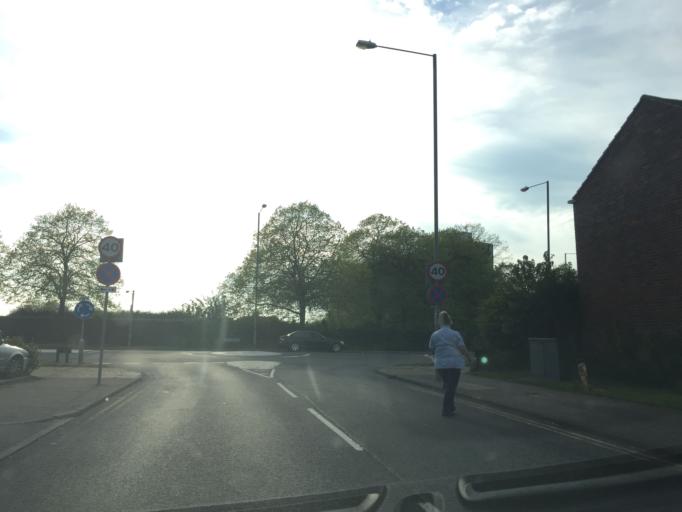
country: GB
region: England
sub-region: Essex
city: Harlow
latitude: 51.7628
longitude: 0.1144
